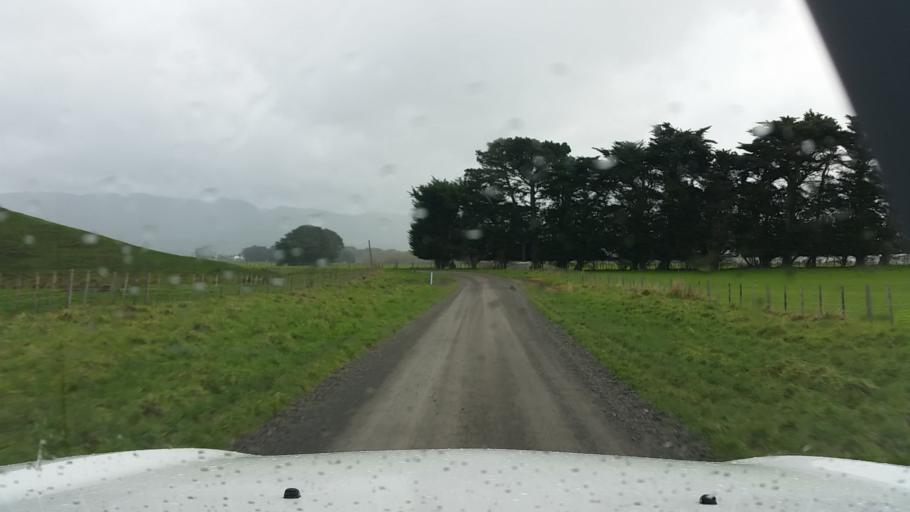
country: NZ
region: Wellington
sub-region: Upper Hutt City
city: Upper Hutt
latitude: -41.3391
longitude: 175.2013
